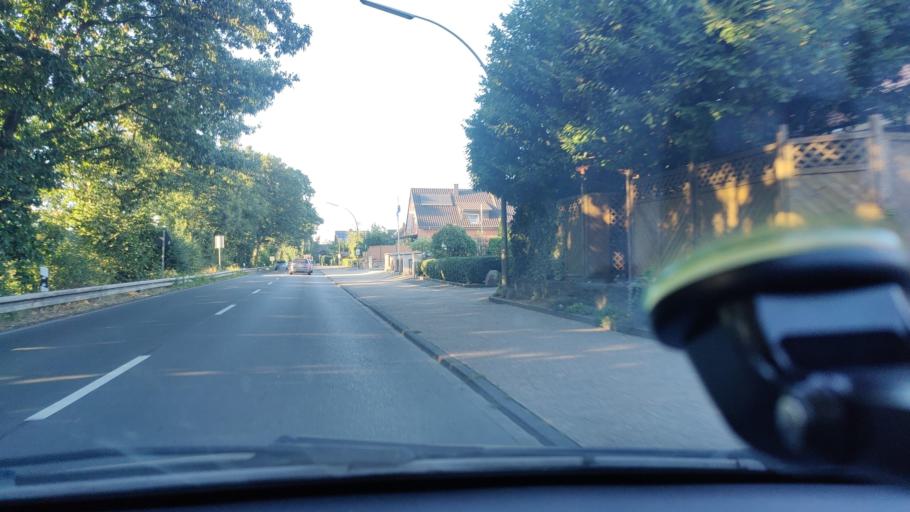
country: DE
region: North Rhine-Westphalia
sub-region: Regierungsbezirk Munster
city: Klein Reken
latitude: 51.7614
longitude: 6.9994
